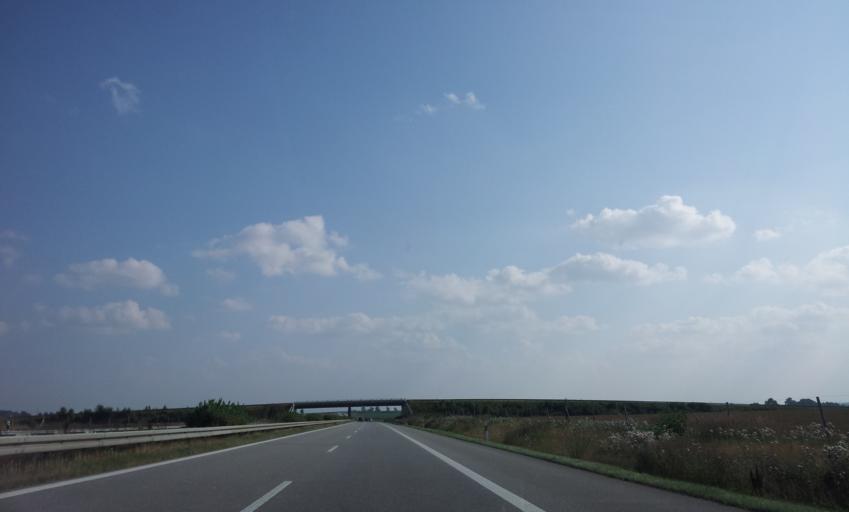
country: DE
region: Mecklenburg-Vorpommern
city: Jarmen
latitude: 53.8409
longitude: 13.3287
